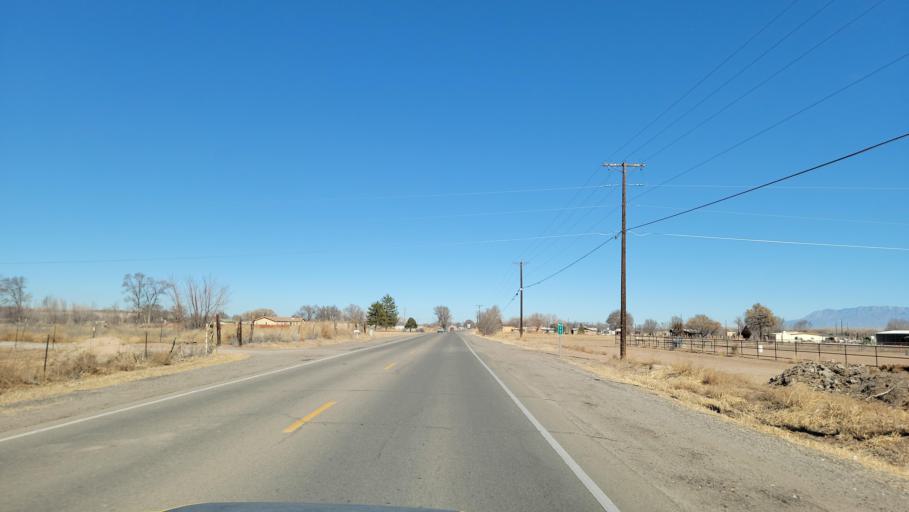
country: US
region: New Mexico
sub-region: Valencia County
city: Bosque Farms
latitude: 34.9283
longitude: -106.6927
